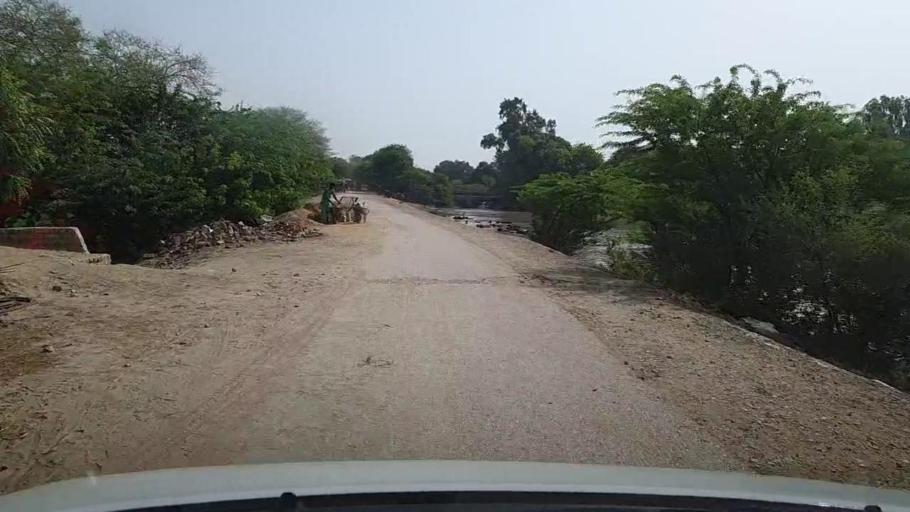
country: PK
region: Sindh
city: Mehar
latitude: 27.1273
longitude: 67.8646
